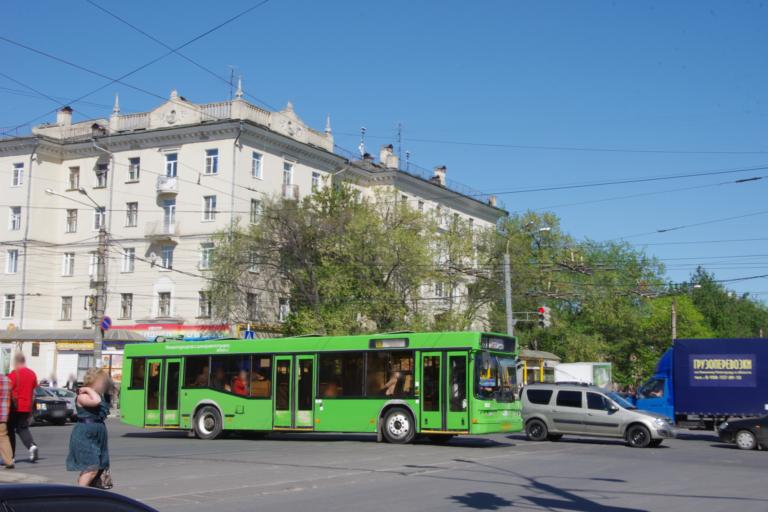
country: RU
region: Nizjnij Novgorod
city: Gorbatovka
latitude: 56.2486
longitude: 43.8649
